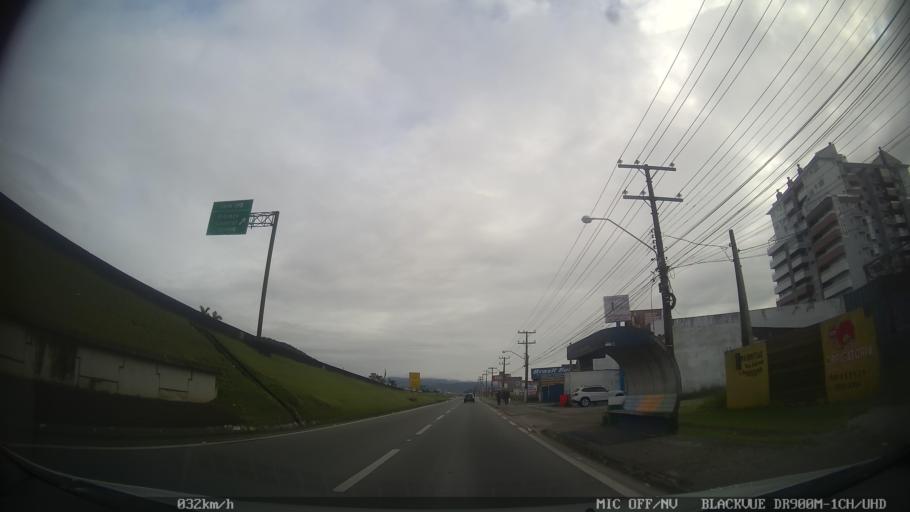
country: BR
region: Santa Catarina
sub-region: Biguacu
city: Biguacu
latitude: -27.5054
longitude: -48.6489
